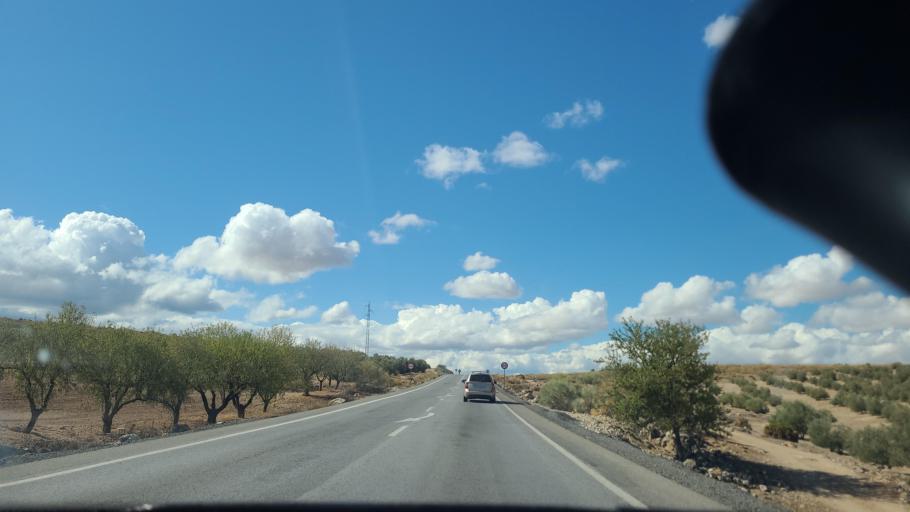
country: ES
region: Andalusia
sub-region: Provincia de Granada
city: Gobernador
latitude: 37.4115
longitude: -3.3479
